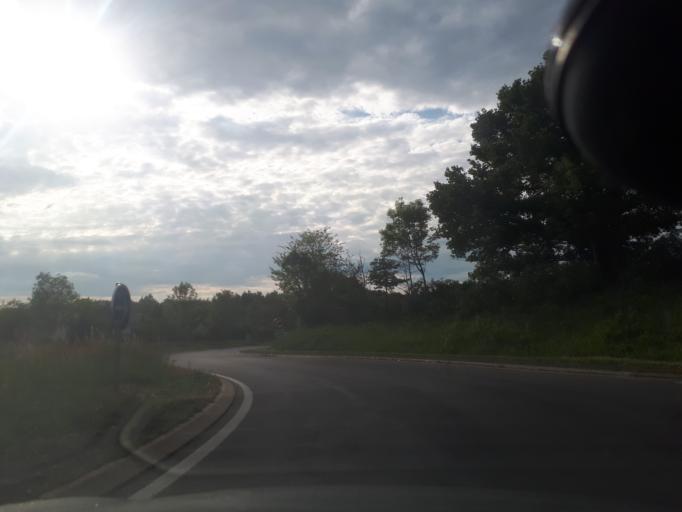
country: FR
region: Auvergne
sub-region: Departement de l'Allier
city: Dompierre-sur-Besbre
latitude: 46.5373
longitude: 3.6551
